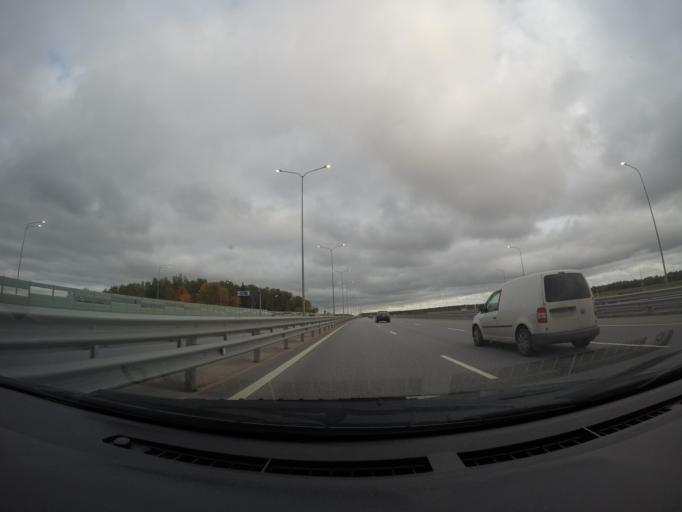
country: RU
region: Moskovskaya
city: Kubinka
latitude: 55.5724
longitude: 36.7113
